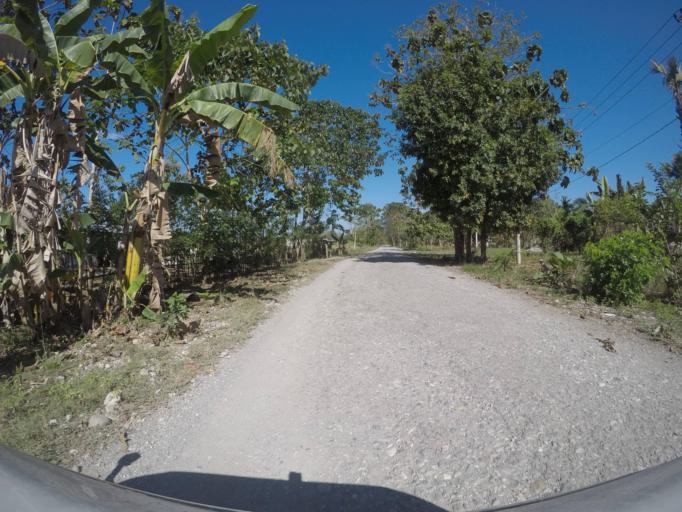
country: TL
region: Viqueque
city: Viqueque
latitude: -8.9338
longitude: 126.1323
